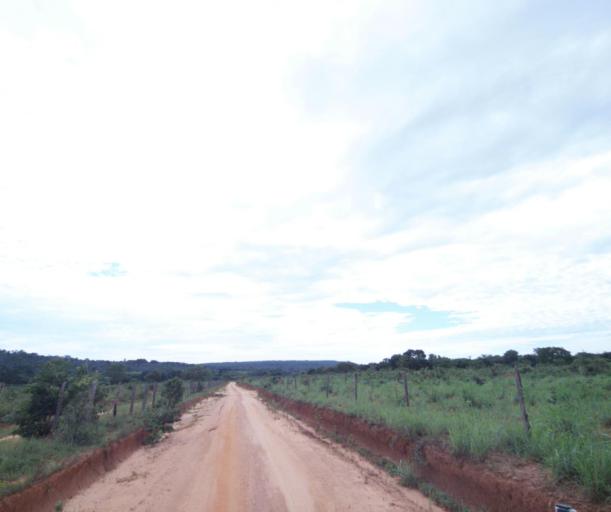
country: BR
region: Bahia
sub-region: Carinhanha
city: Carinhanha
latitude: -14.2081
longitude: -44.4617
